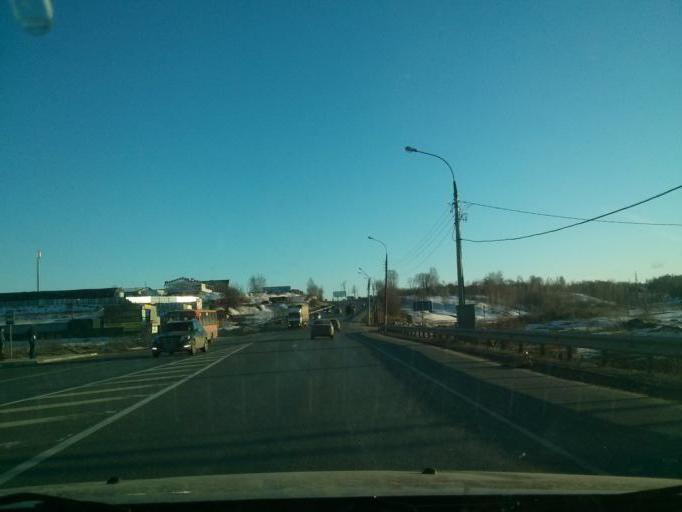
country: RU
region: Nizjnij Novgorod
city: Afonino
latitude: 56.2362
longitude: 44.0989
